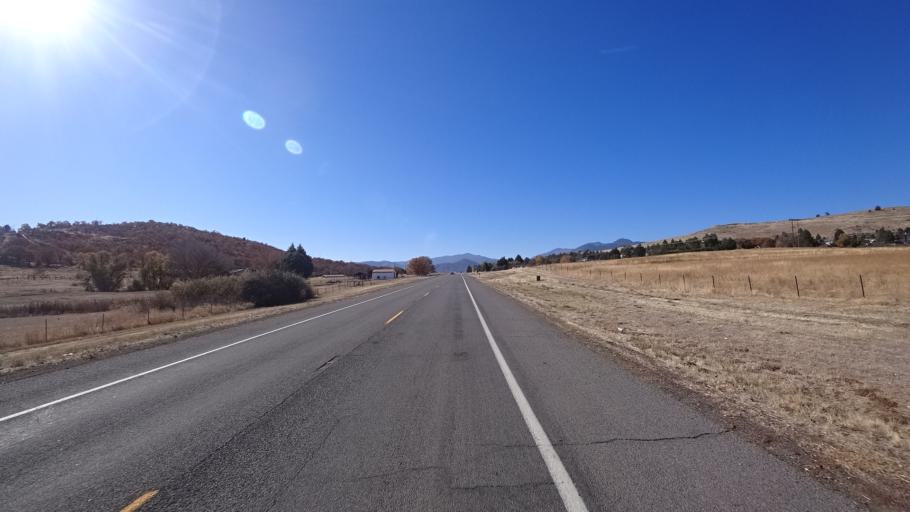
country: US
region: California
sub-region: Siskiyou County
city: Yreka
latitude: 41.7415
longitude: -122.6069
